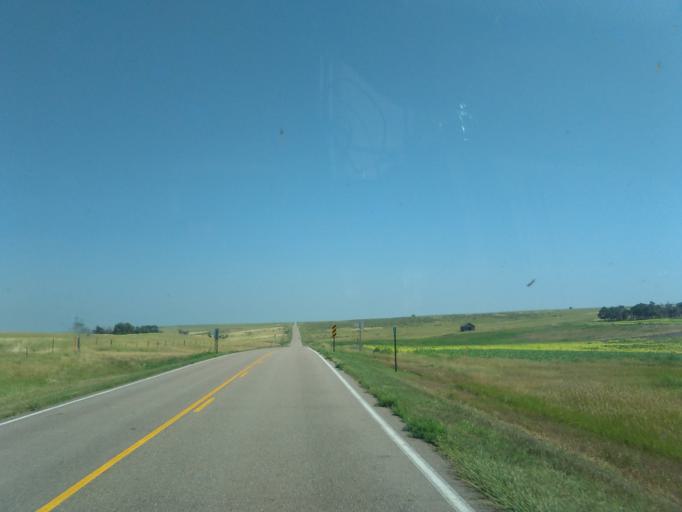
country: US
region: Nebraska
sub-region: Dundy County
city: Benkelman
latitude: 39.9301
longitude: -101.5413
